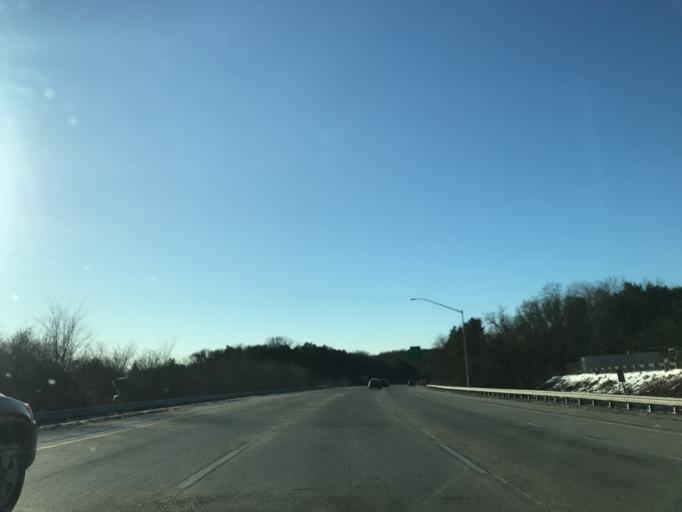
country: US
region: Maryland
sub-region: Anne Arundel County
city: South Gate
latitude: 39.0877
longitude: -76.6251
